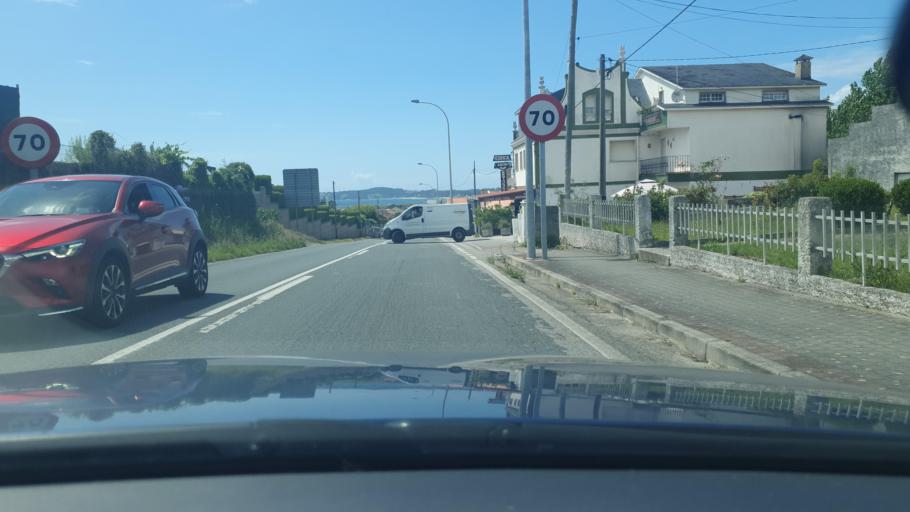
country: ES
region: Galicia
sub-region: Provincia de Pontevedra
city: O Grove
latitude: 42.4401
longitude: -8.8490
